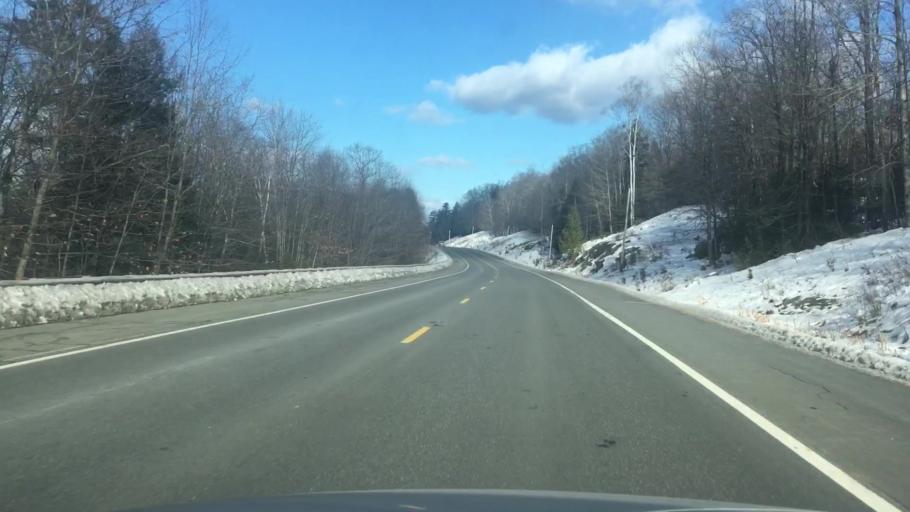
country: US
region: Maine
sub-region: Somerset County
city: Madison
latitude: 45.0023
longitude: -69.8582
